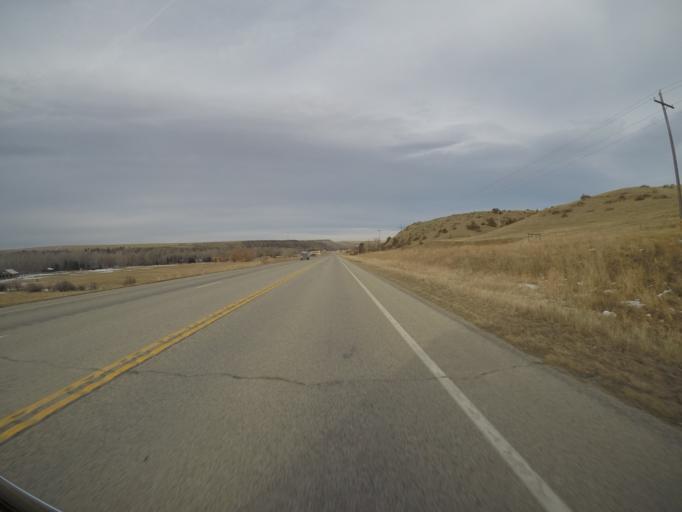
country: US
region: Montana
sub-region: Stillwater County
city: Absarokee
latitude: 45.5004
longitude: -109.4489
